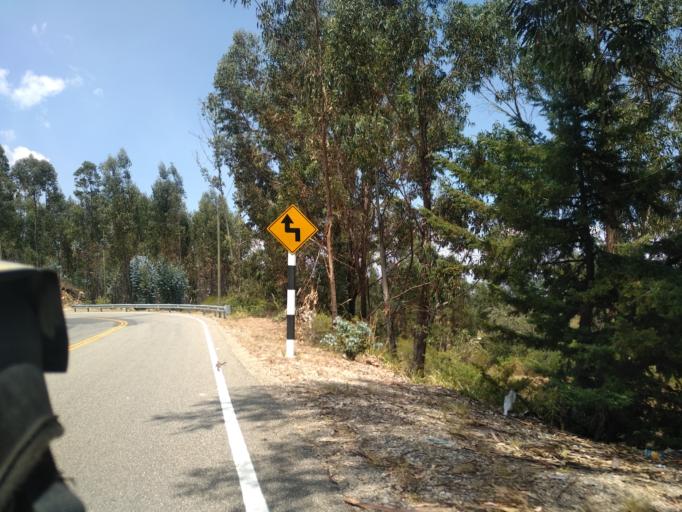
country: PE
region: Cajamarca
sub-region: San Marcos
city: San Marcos
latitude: -7.2867
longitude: -78.2071
